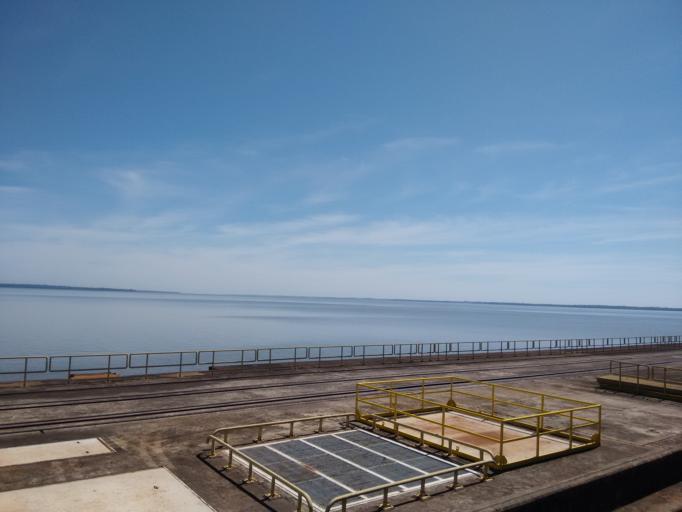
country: PY
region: Alto Parana
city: Ciudad del Este
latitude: -25.4078
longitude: -54.5871
